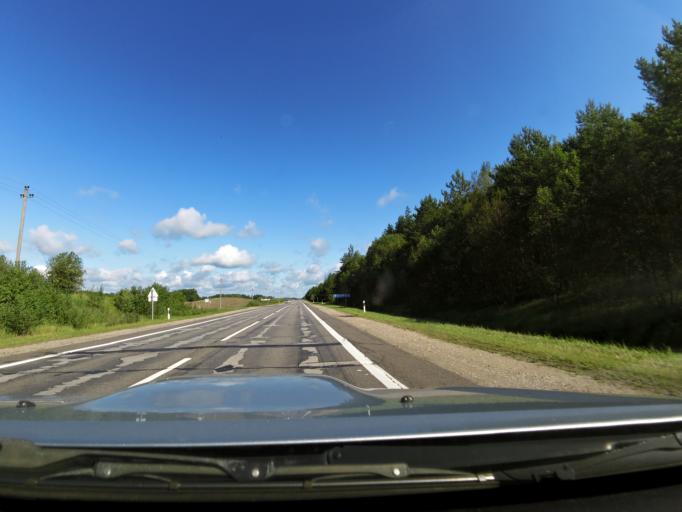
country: LT
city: Moletai
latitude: 55.3187
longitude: 25.5147
